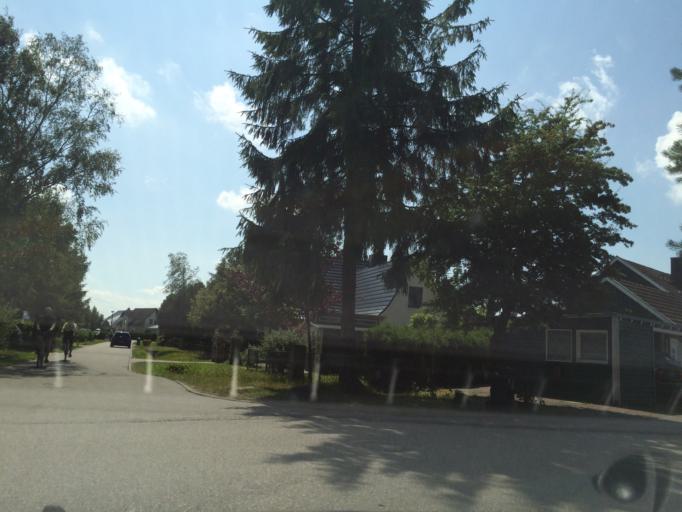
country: DE
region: Mecklenburg-Vorpommern
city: Zingst
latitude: 54.4318
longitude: 12.6795
